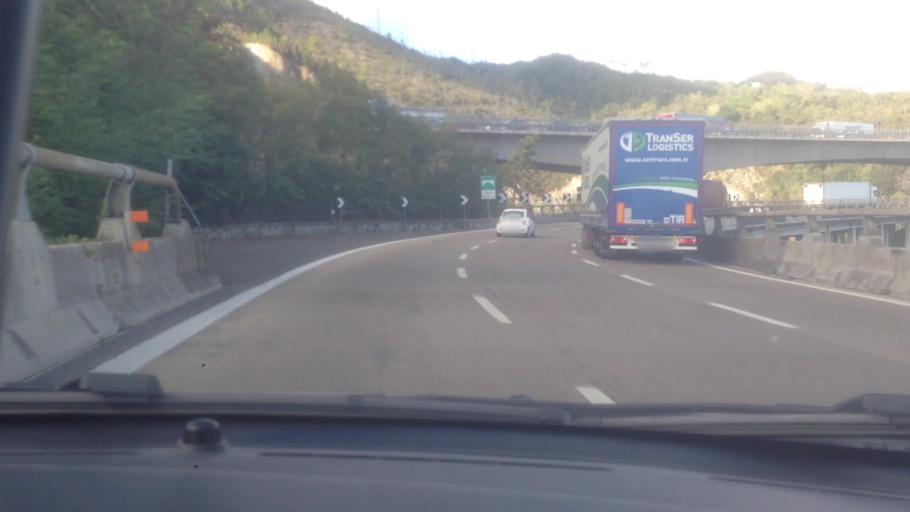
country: IT
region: Liguria
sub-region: Provincia di Genova
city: Arenzano
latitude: 44.4149
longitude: 8.7028
